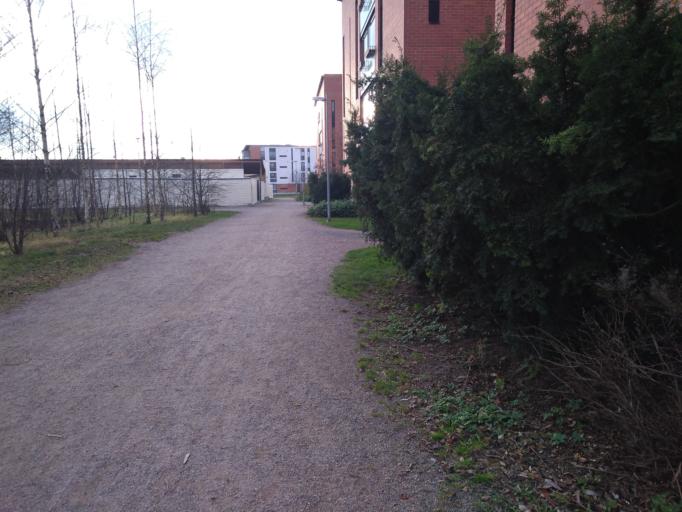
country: FI
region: Uusimaa
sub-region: Helsinki
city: Vantaa
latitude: 60.2308
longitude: 25.0331
